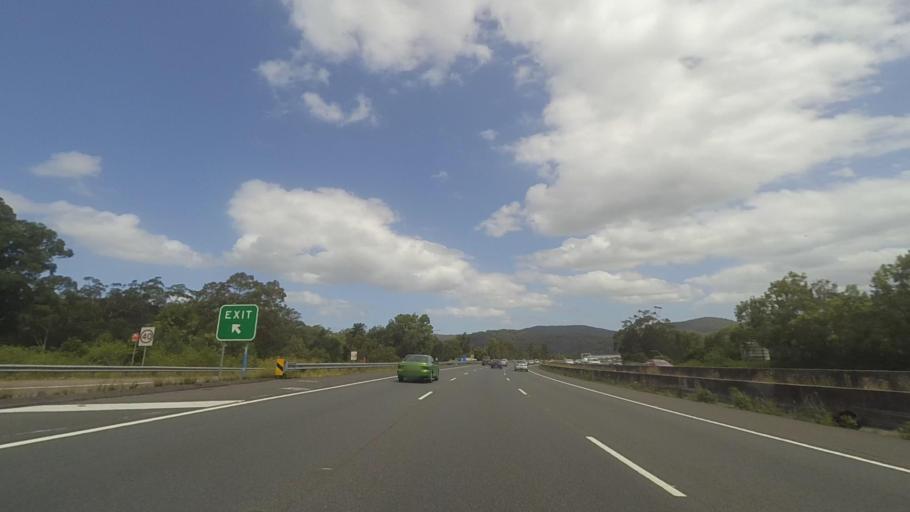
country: AU
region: New South Wales
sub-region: Hornsby Shire
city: Berowra Heights
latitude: -33.5281
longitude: 151.1992
